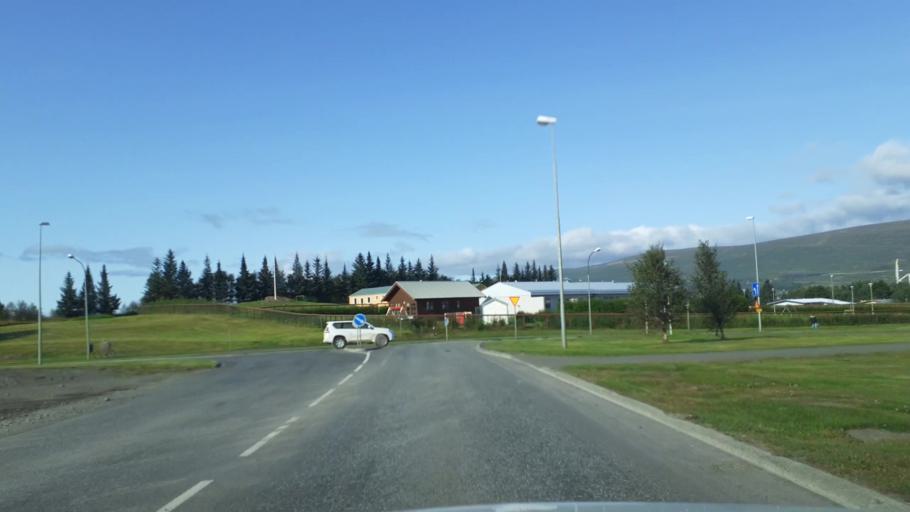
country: IS
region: Northeast
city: Akureyri
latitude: 65.6772
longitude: -18.1286
